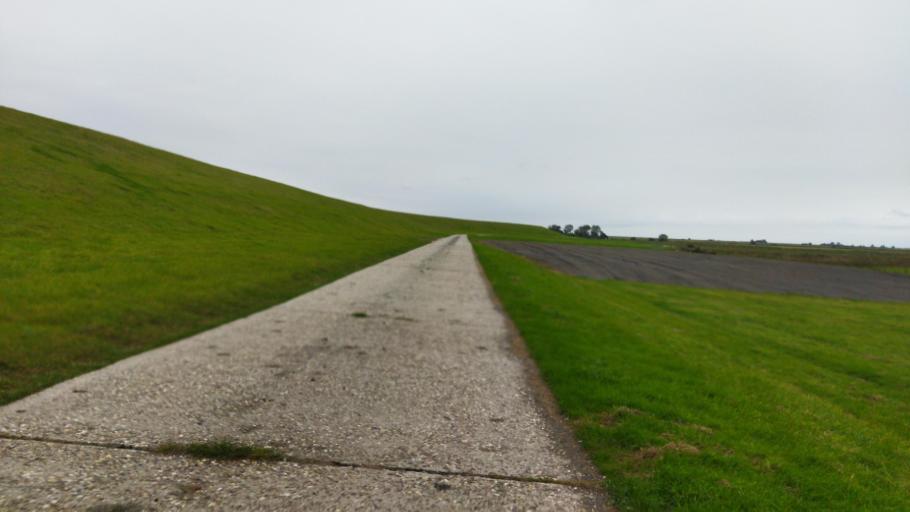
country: DE
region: Lower Saxony
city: Wirdum
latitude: 53.4908
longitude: 7.0384
